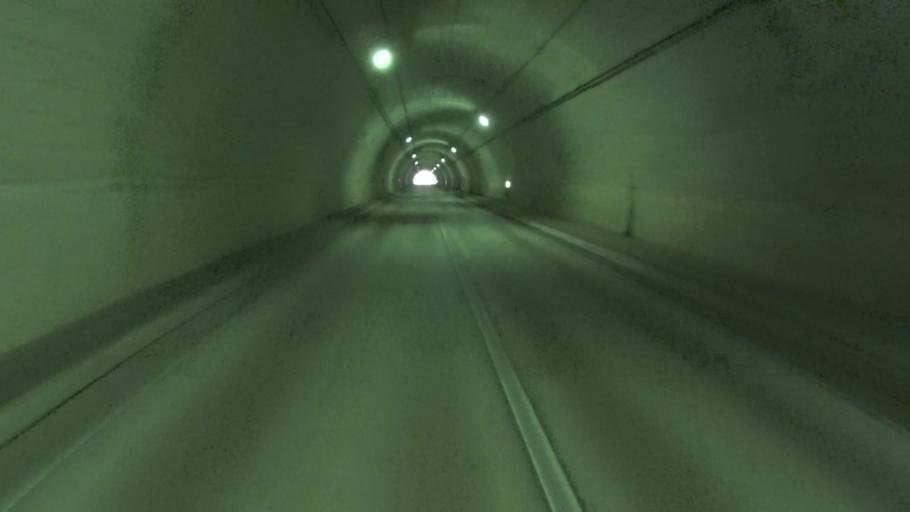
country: JP
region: Kyoto
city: Miyazu
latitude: 35.7291
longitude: 135.0933
